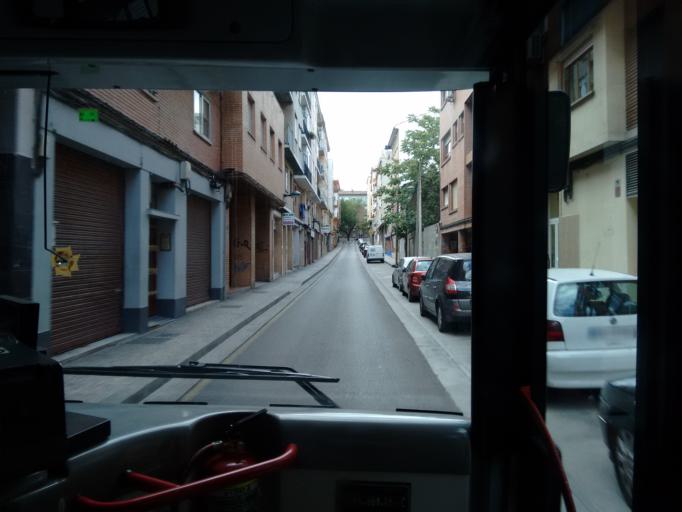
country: ES
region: Aragon
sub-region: Provincia de Zaragoza
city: Zaragoza
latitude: 41.6278
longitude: -0.8834
